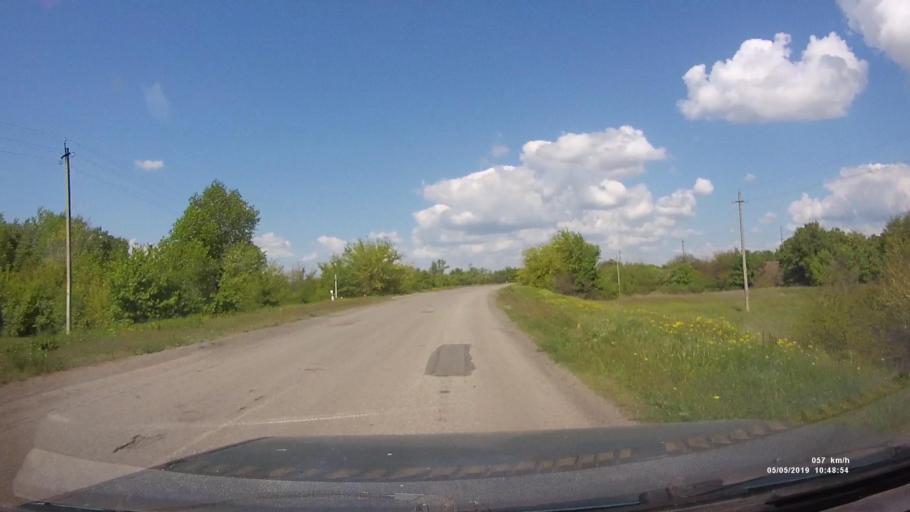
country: RU
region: Rostov
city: Ust'-Donetskiy
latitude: 47.6451
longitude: 40.8135
